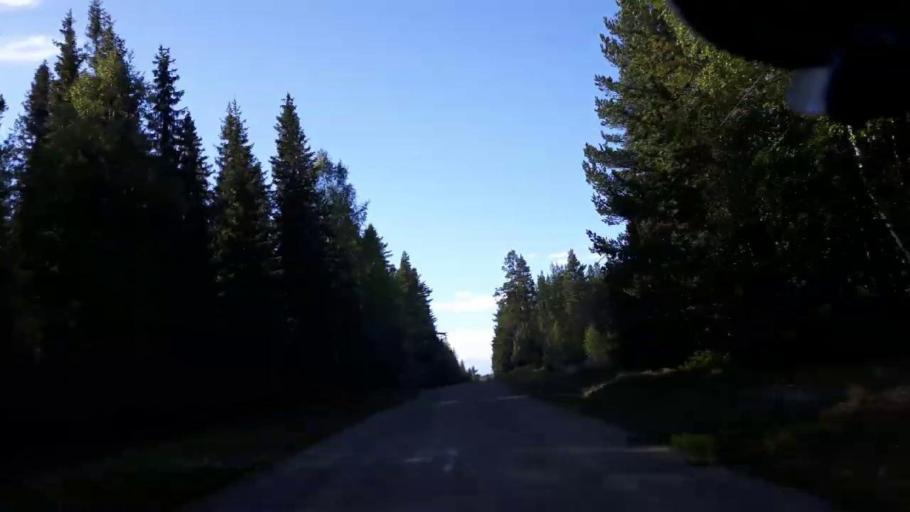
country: SE
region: Jaemtland
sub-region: Ragunda Kommun
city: Hammarstrand
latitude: 63.4812
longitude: 16.1225
